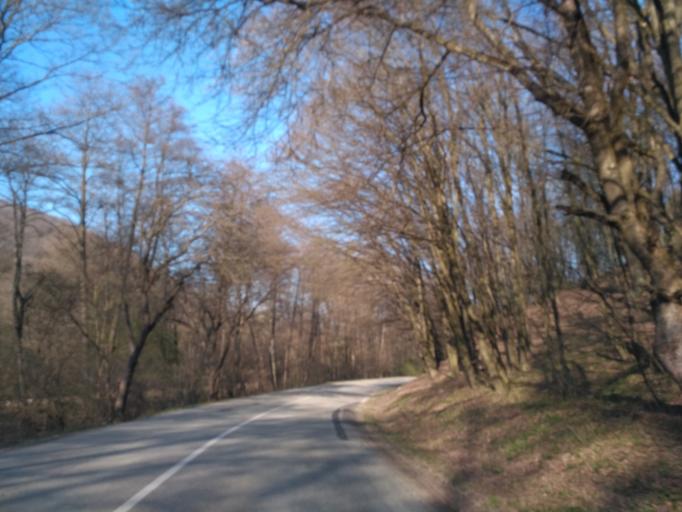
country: SK
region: Kosicky
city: Medzev
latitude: 48.6926
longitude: 20.9502
